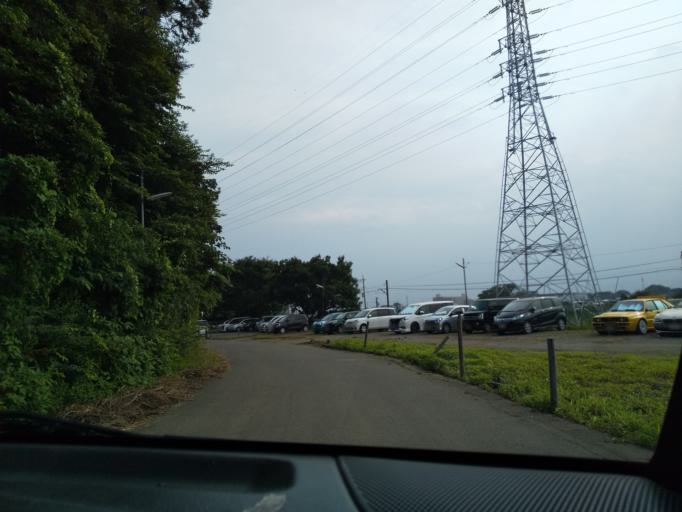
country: JP
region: Kanagawa
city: Zama
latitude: 35.4724
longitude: 139.3958
